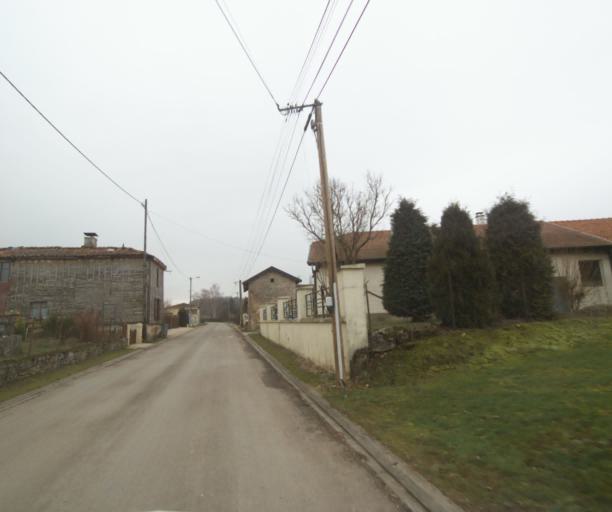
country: FR
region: Champagne-Ardenne
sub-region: Departement de la Haute-Marne
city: Wassy
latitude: 48.5419
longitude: 4.9807
